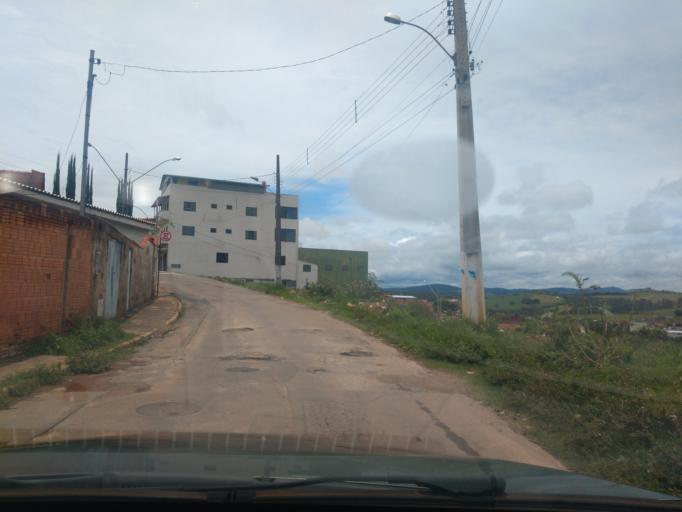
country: BR
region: Minas Gerais
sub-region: Tres Coracoes
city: Tres Coracoes
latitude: -21.6909
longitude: -45.2495
